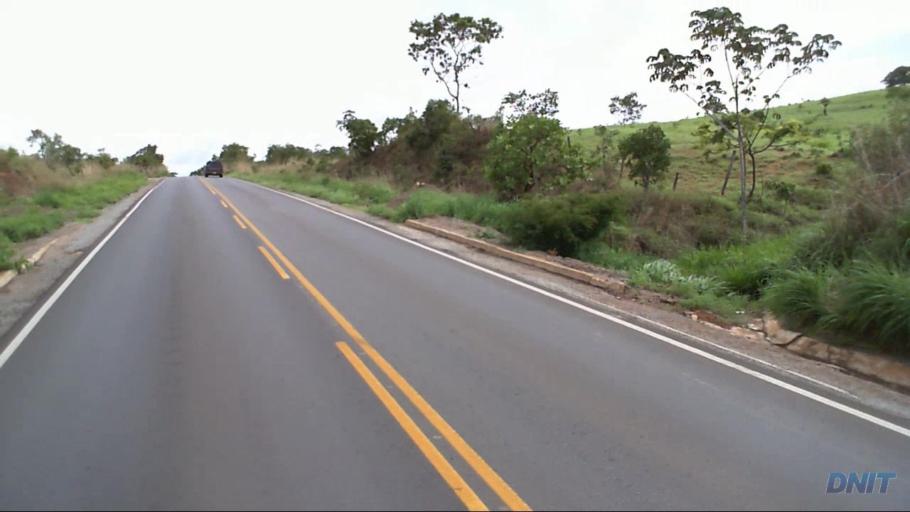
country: BR
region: Goias
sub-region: Padre Bernardo
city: Padre Bernardo
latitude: -15.2118
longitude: -48.2816
